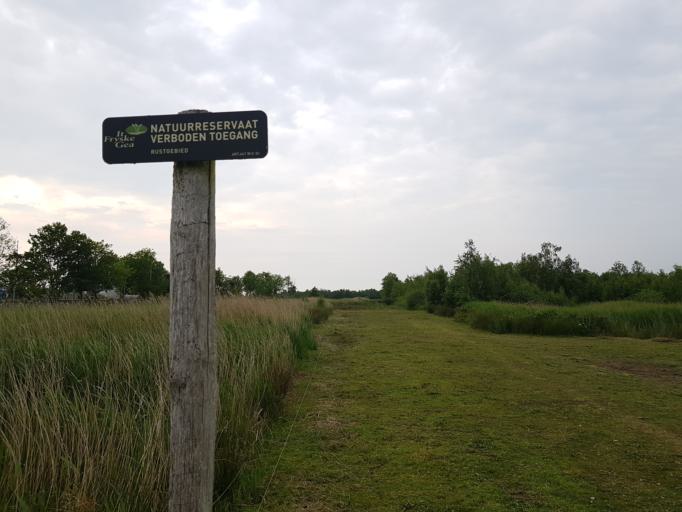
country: NL
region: Friesland
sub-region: Gemeente Tytsjerksteradiel
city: Garyp
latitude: 53.1354
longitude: 5.9394
